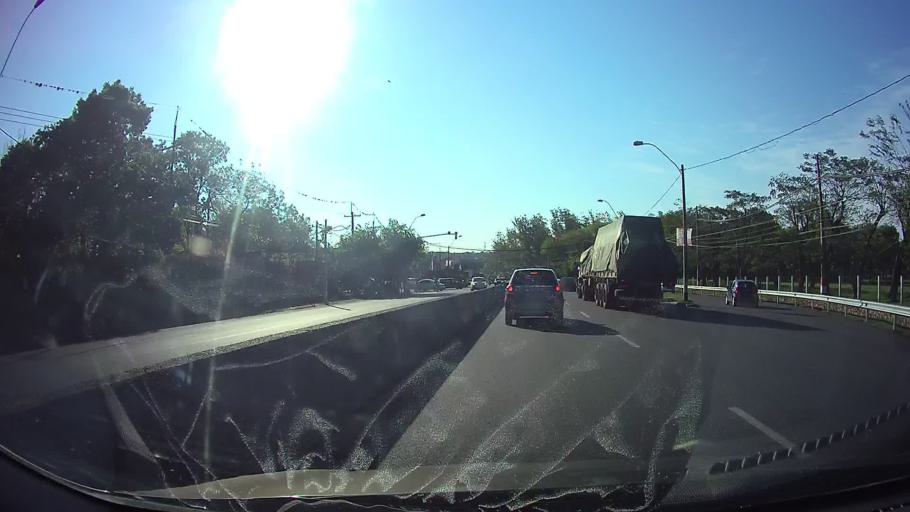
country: PY
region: Central
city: Capiata
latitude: -25.3609
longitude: -57.4310
